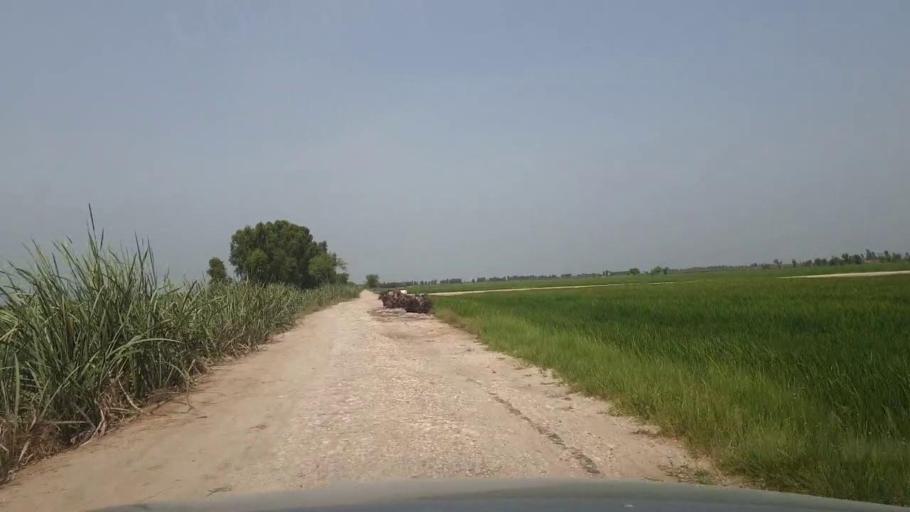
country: PK
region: Sindh
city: Garhi Yasin
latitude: 27.9372
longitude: 68.4313
